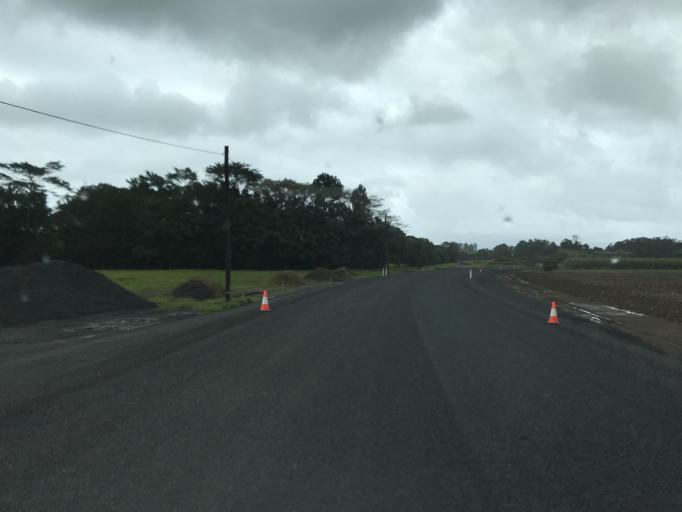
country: AU
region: Queensland
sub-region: Cassowary Coast
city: Innisfail
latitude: -17.5031
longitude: 145.9919
